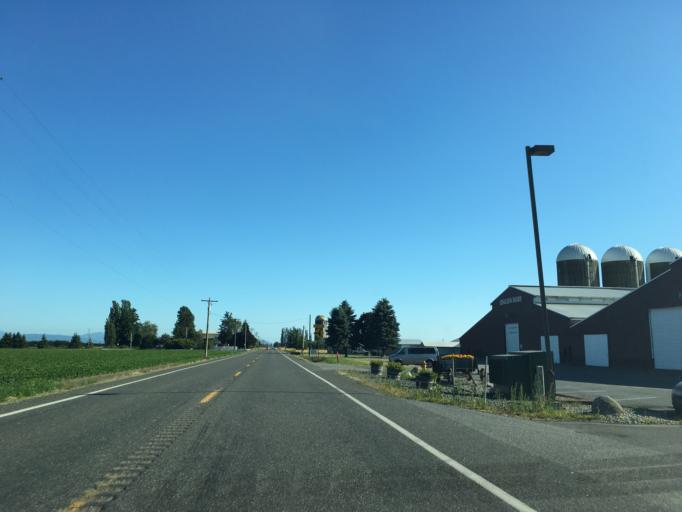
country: US
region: Washington
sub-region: Whatcom County
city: Lynden
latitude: 48.9888
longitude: -122.4852
